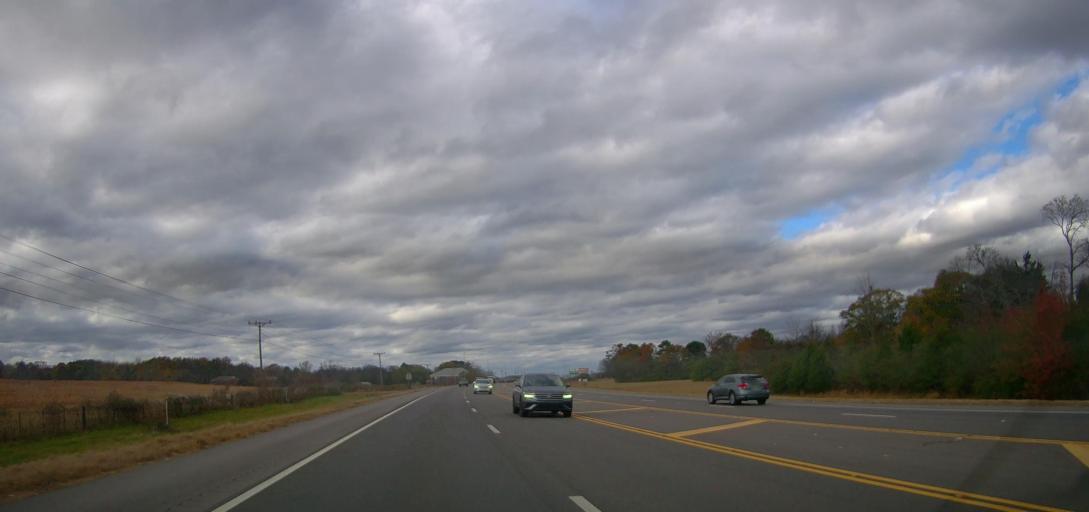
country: US
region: Alabama
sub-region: Lawrence County
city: Moulton
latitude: 34.4709
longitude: -87.2663
